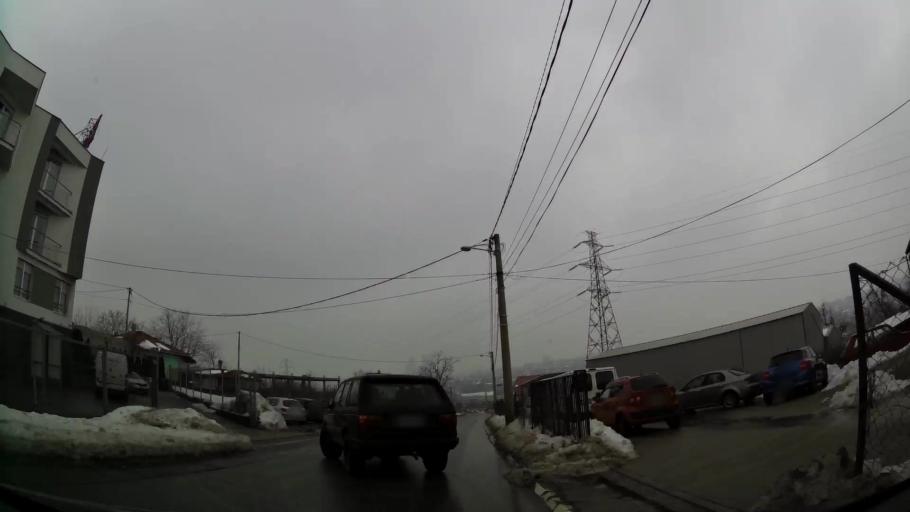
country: RS
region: Central Serbia
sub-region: Belgrade
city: Zvezdara
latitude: 44.7687
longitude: 20.5174
